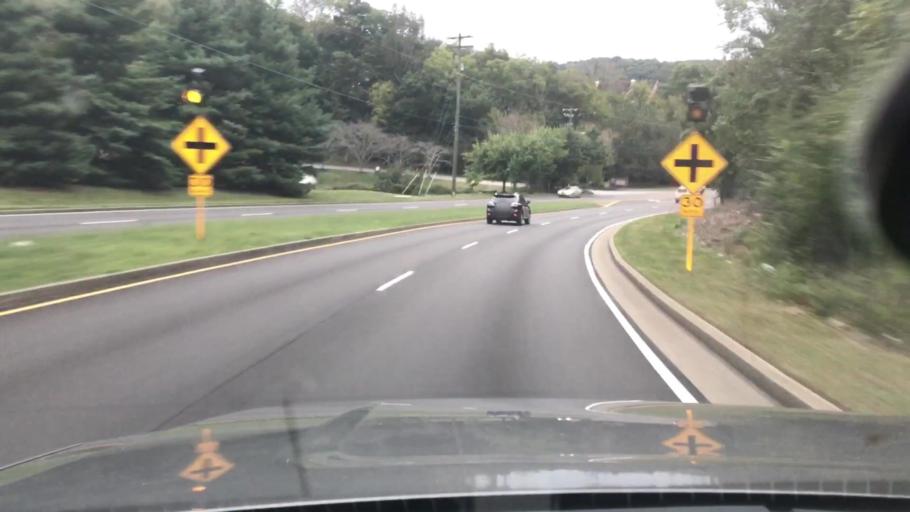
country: US
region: Tennessee
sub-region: Davidson County
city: Belle Meade
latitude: 36.0679
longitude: -86.9173
